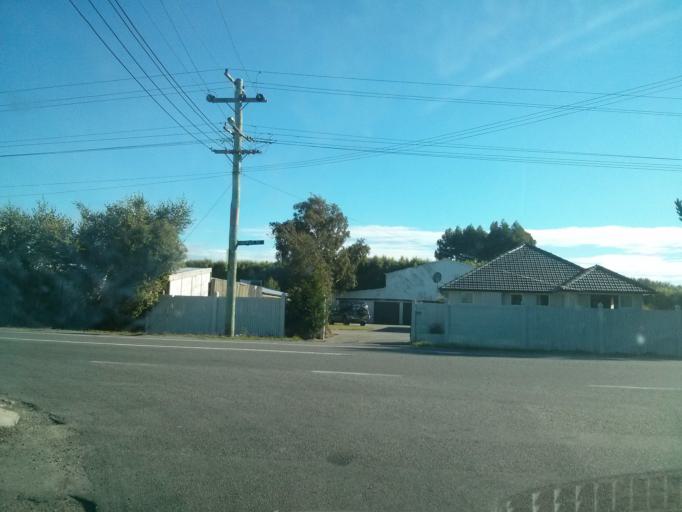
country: NZ
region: Canterbury
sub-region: Christchurch City
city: Christchurch
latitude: -43.4799
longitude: 172.5624
